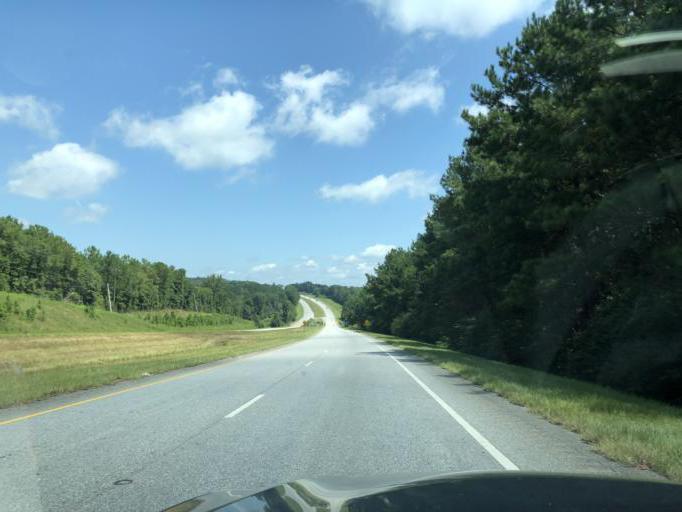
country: US
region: Alabama
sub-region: Barbour County
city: Eufaula
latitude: 31.7696
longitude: -85.1879
